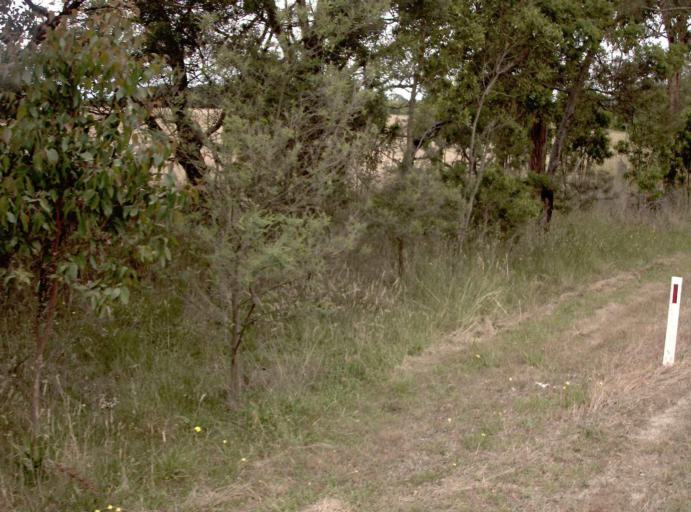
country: AU
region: Victoria
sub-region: Latrobe
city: Traralgon
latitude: -38.4928
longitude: 146.8190
